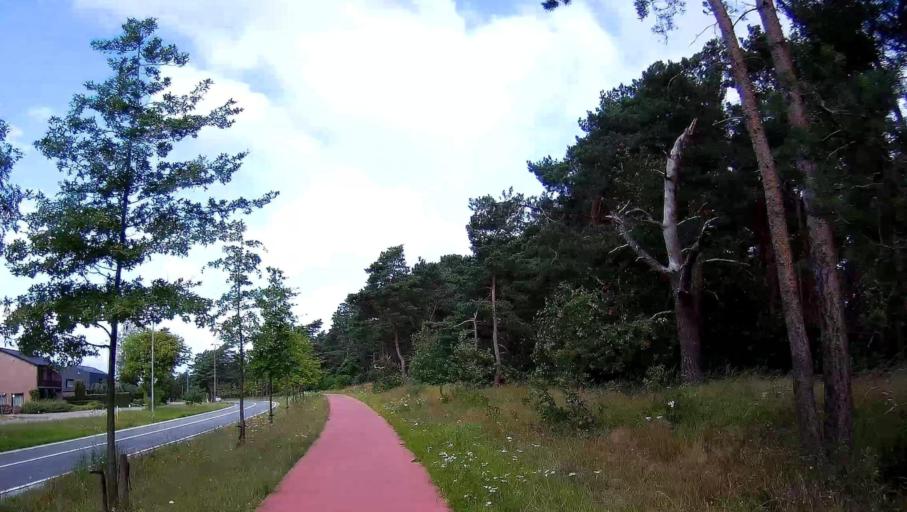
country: BE
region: Flanders
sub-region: Provincie Limburg
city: Lommel
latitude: 51.2334
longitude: 5.2847
